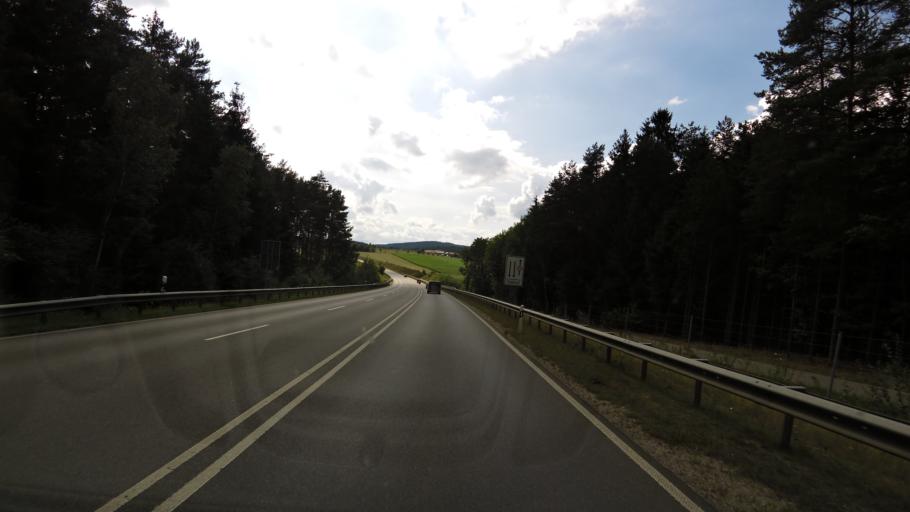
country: DE
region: Bavaria
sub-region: Upper Palatinate
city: Weiding
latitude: 49.2699
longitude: 12.7626
